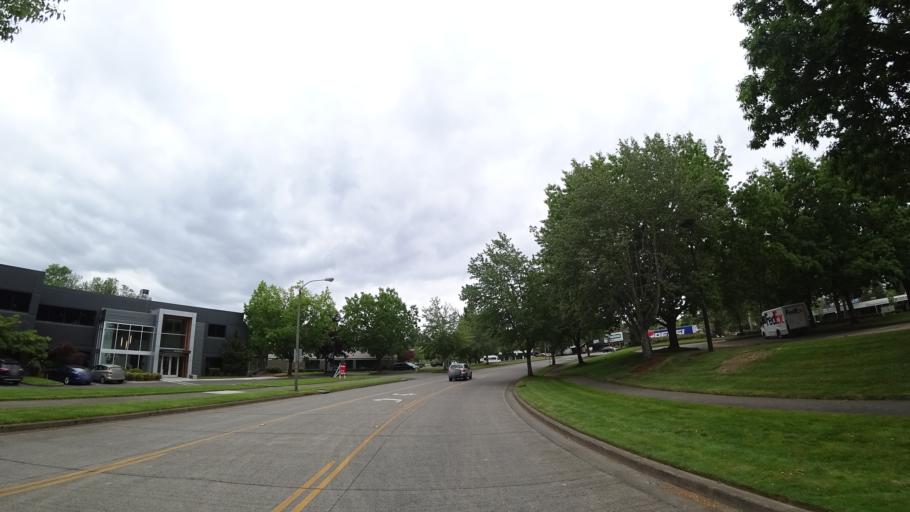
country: US
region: Oregon
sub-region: Washington County
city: Beaverton
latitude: 45.4594
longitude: -122.7929
